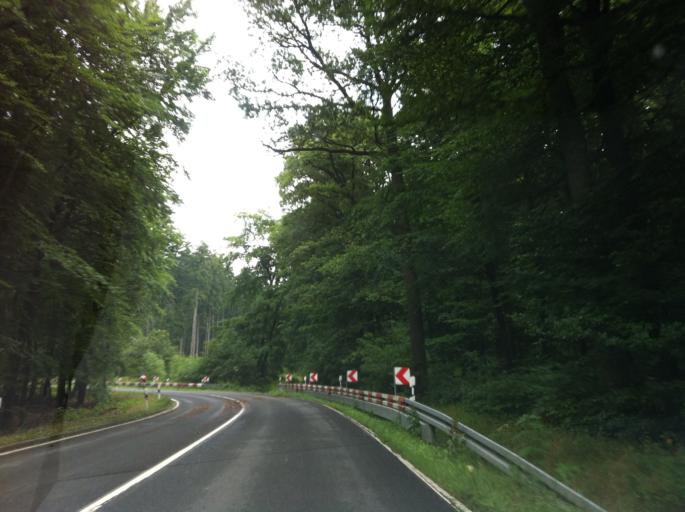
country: DE
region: Hesse
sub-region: Regierungsbezirk Darmstadt
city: Glashutten
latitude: 50.2078
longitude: 8.4359
